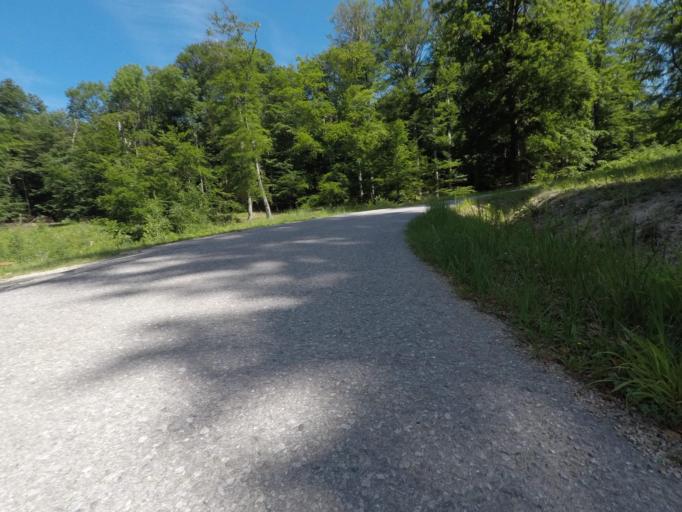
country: AT
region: Lower Austria
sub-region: Politischer Bezirk Modling
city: Perchtoldsdorf
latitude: 48.1759
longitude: 16.2387
